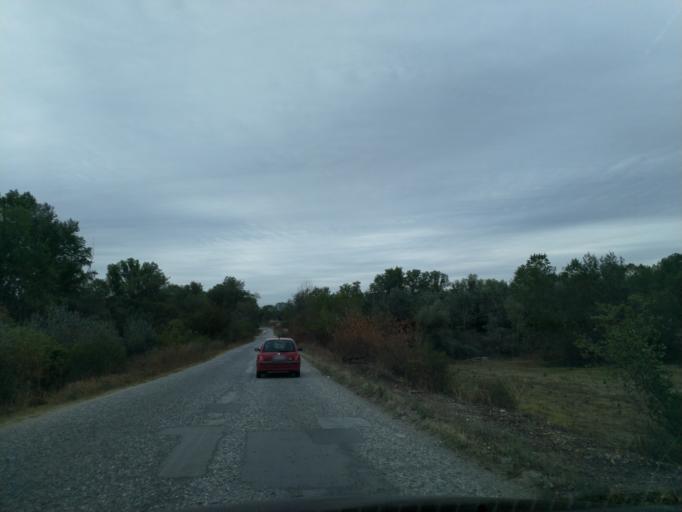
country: RS
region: Central Serbia
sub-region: Pomoravski Okrug
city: Paracin
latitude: 43.8278
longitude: 21.3464
